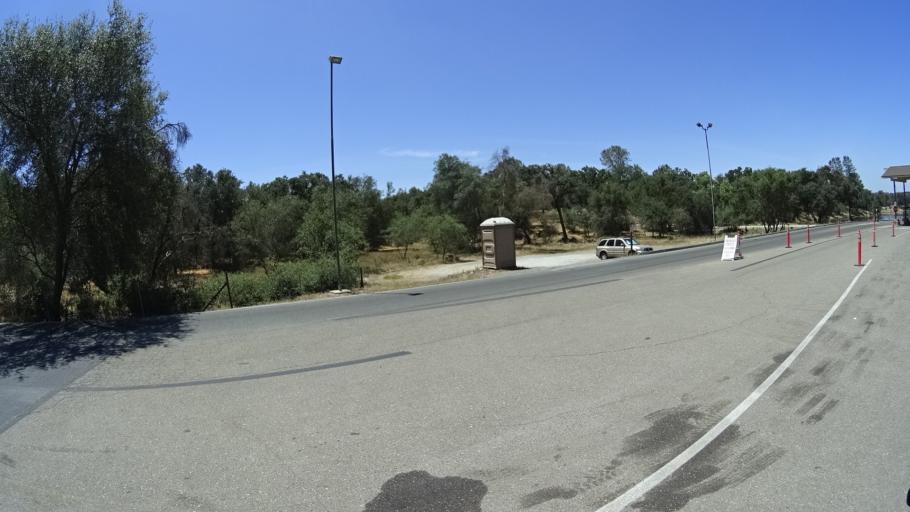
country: US
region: California
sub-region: Calaveras County
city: Valley Springs
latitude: 38.2112
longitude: -120.9171
